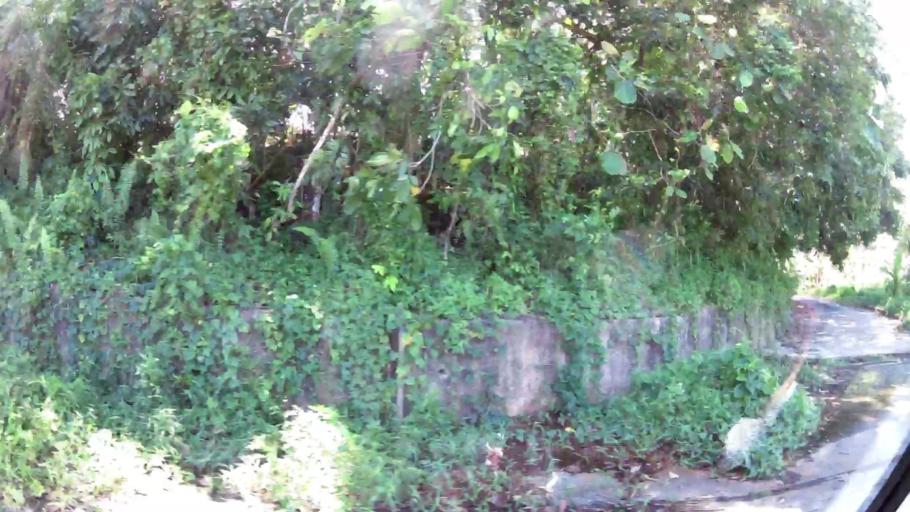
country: BN
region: Brunei and Muara
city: Bandar Seri Begawan
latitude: 4.9334
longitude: 114.9557
